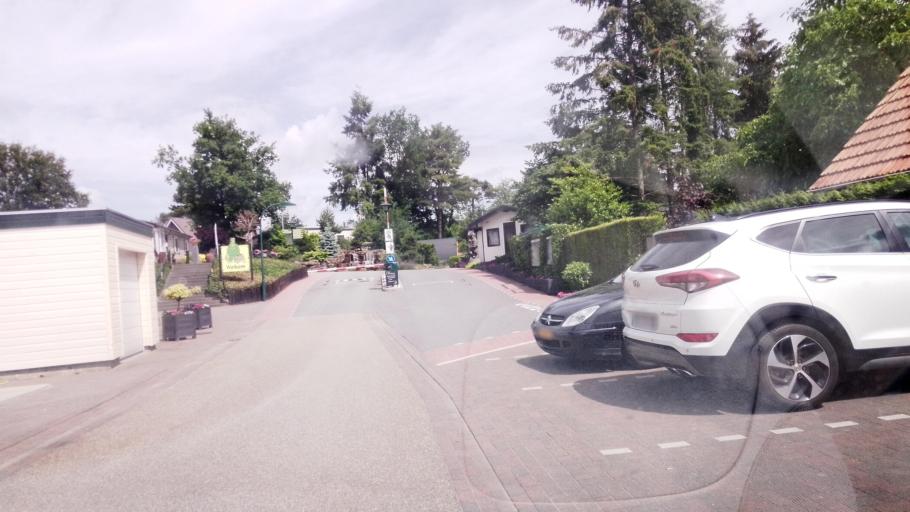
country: NL
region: North Brabant
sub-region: Gemeente Boxmeer
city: Boxmeer
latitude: 51.6346
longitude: 6.0342
